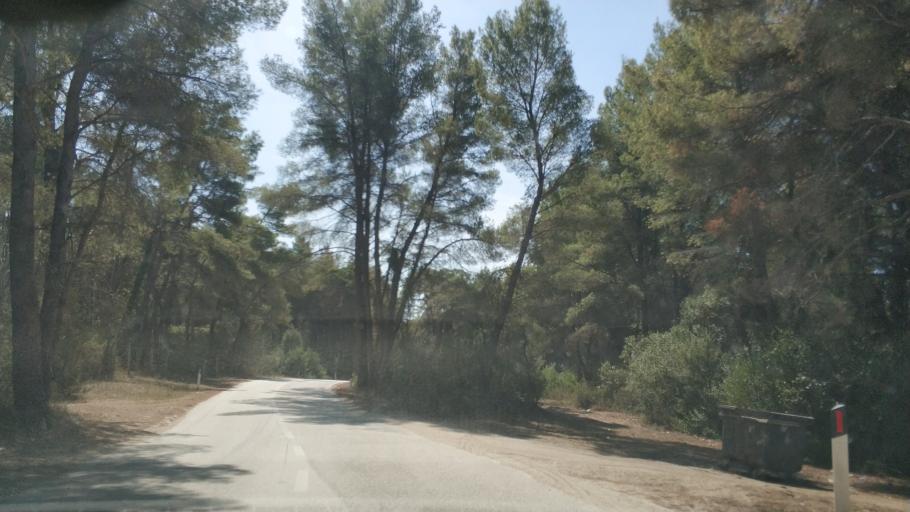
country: AL
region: Fier
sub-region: Rrethi i Lushnjes
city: Divjake
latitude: 40.9804
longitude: 19.4820
